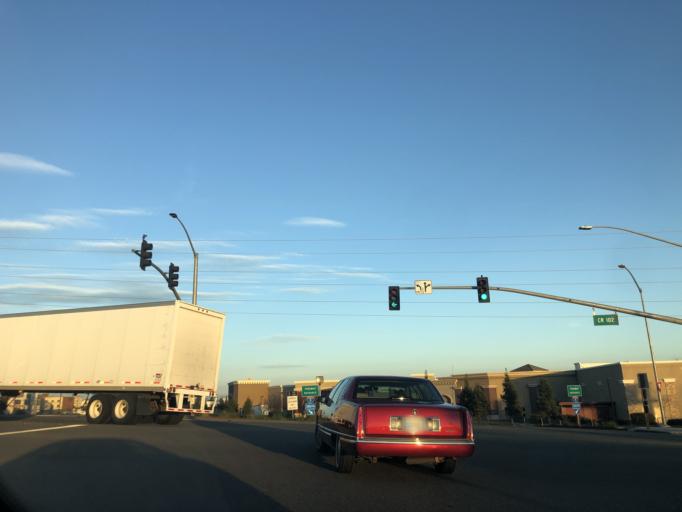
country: US
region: California
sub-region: Yolo County
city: Woodland
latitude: 38.6724
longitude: -121.7288
